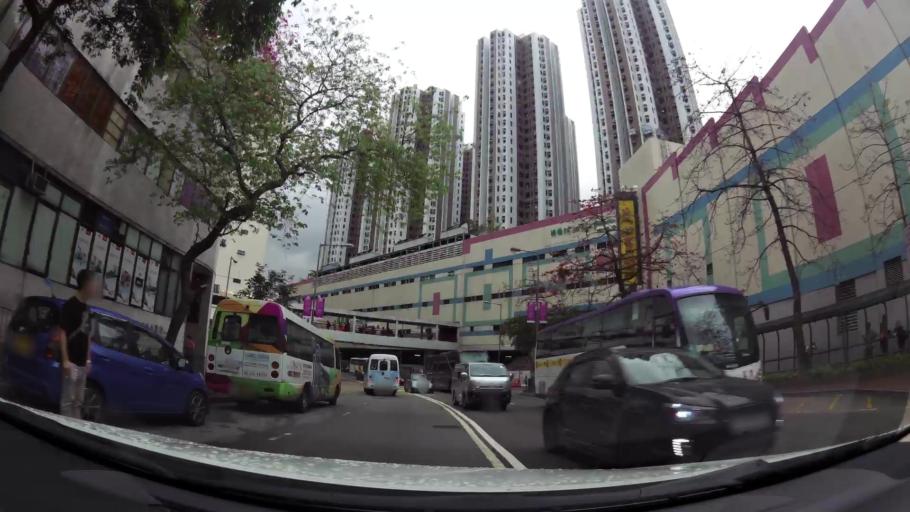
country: HK
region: Tsuen Wan
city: Tsuen Wan
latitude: 22.3723
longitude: 114.1195
